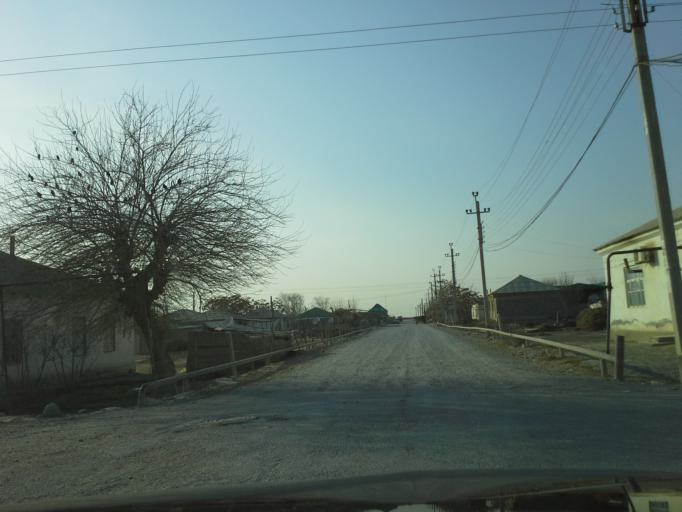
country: TM
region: Ahal
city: Abadan
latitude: 38.1739
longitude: 58.0417
